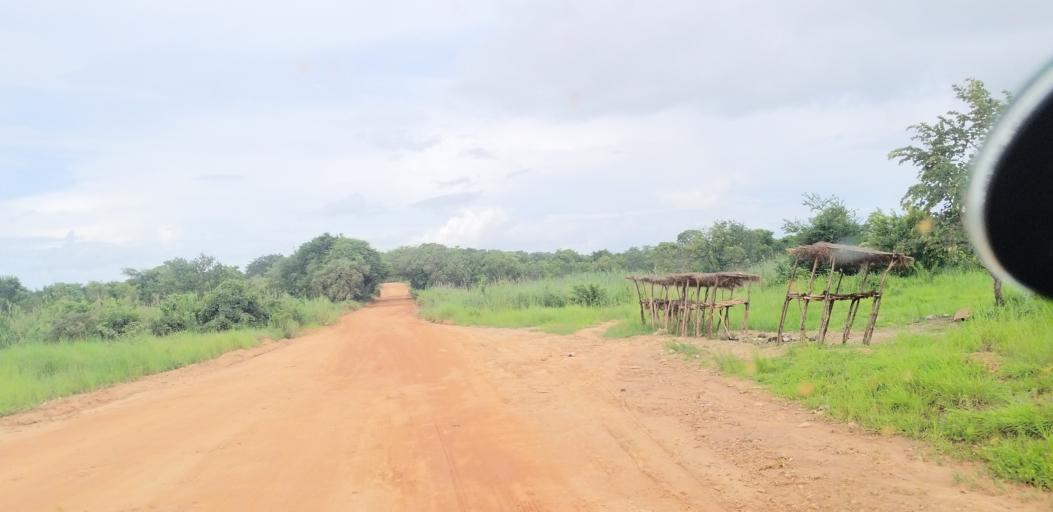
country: ZM
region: Lusaka
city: Lusaka
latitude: -15.1956
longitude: 28.4435
